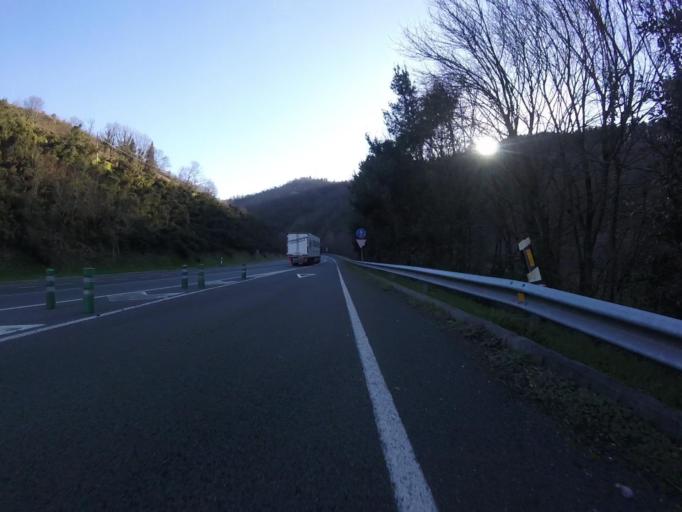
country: ES
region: Navarre
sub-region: Provincia de Navarra
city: Bera
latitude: 43.2647
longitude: -1.6853
